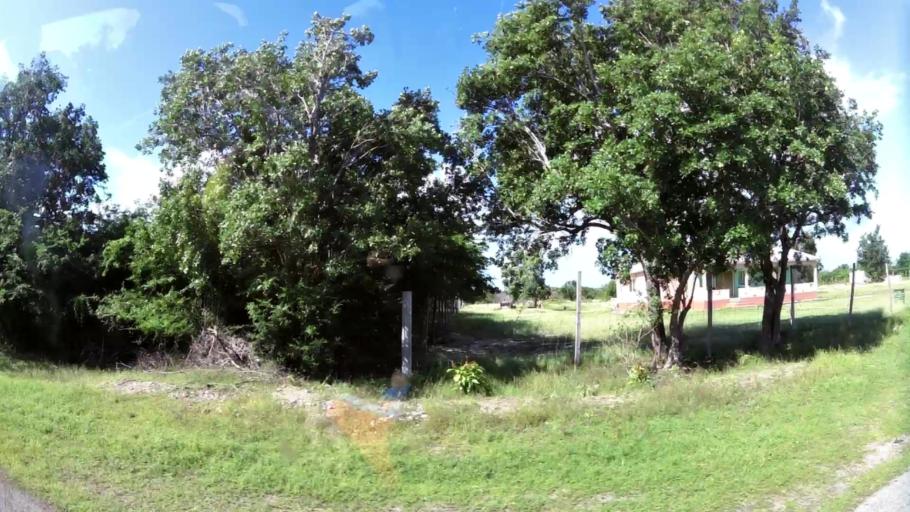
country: AG
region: Barbuda
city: Codrington
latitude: 17.6155
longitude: -61.8283
